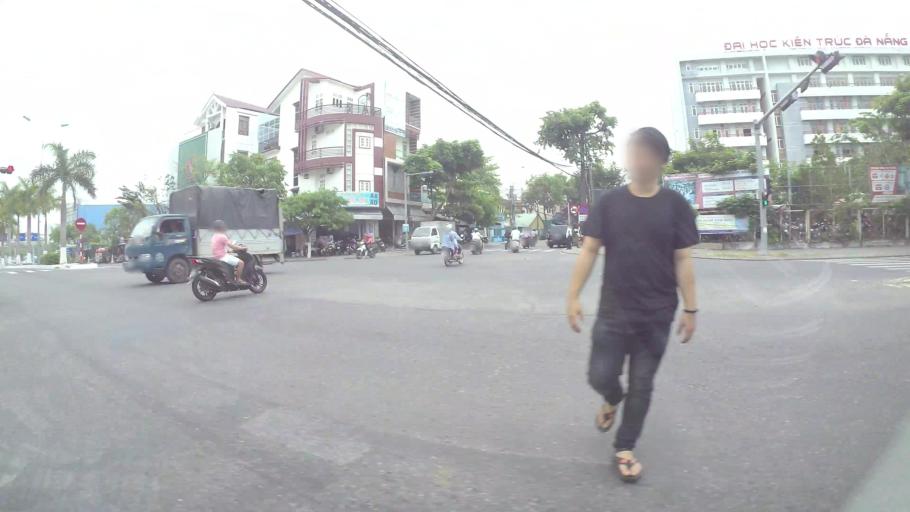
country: VN
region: Da Nang
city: Cam Le
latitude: 16.0328
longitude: 108.2227
